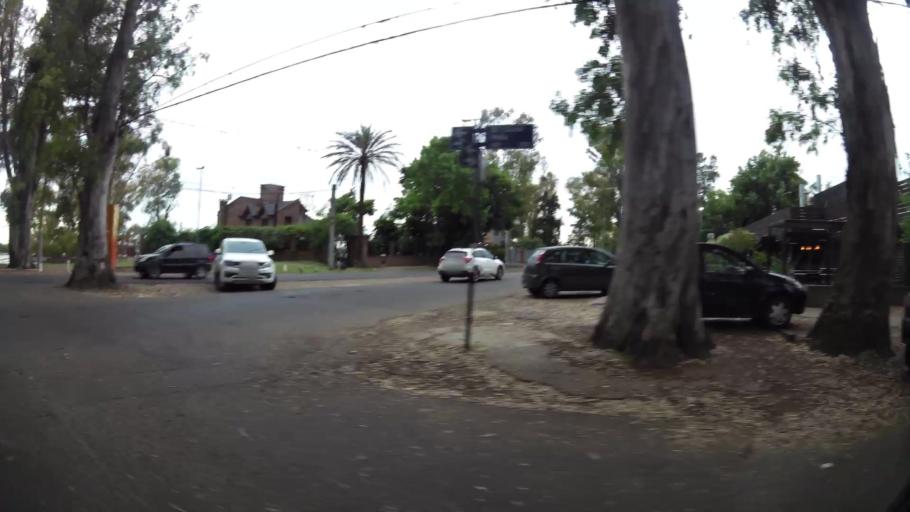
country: AR
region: Santa Fe
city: Granadero Baigorria
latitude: -32.8774
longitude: -60.6881
